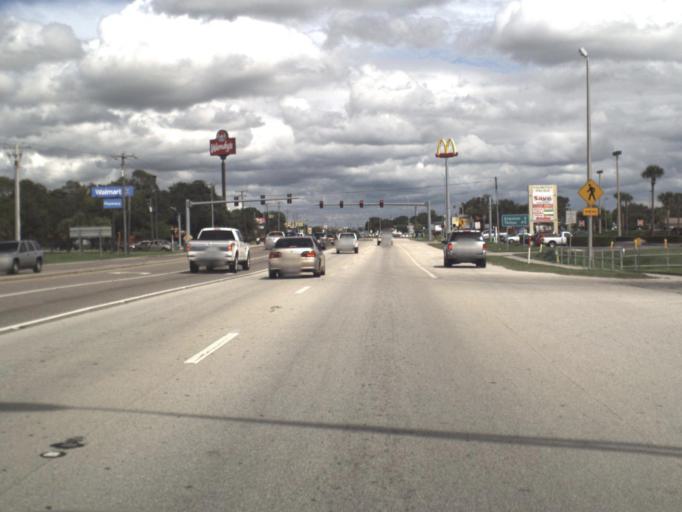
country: US
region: Florida
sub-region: Manatee County
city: Palmetto
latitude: 27.5211
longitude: -82.5609
